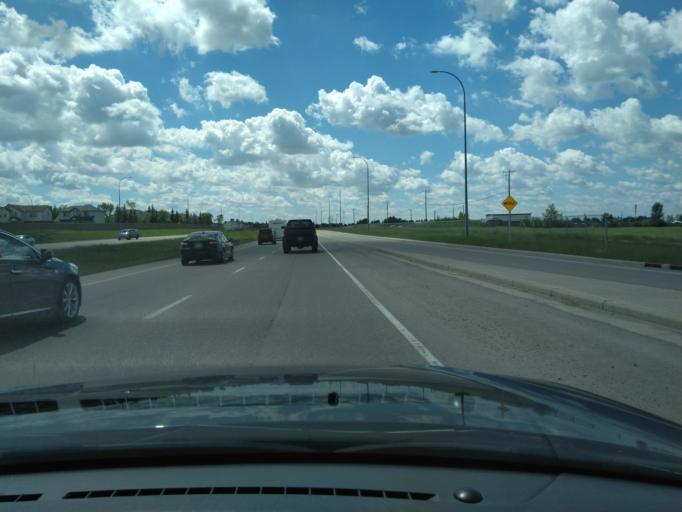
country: CA
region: Alberta
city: Calgary
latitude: 51.1246
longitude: -113.9704
